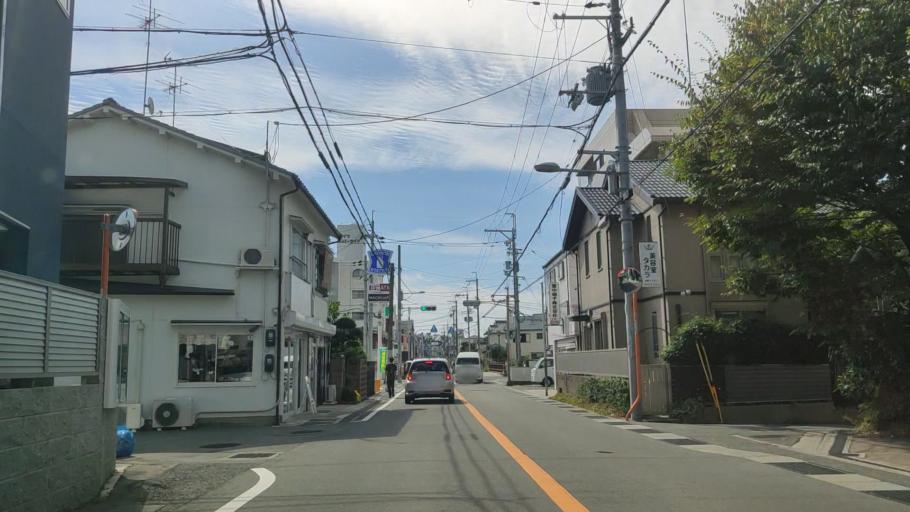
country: JP
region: Osaka
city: Toyonaka
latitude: 34.7963
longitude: 135.4642
